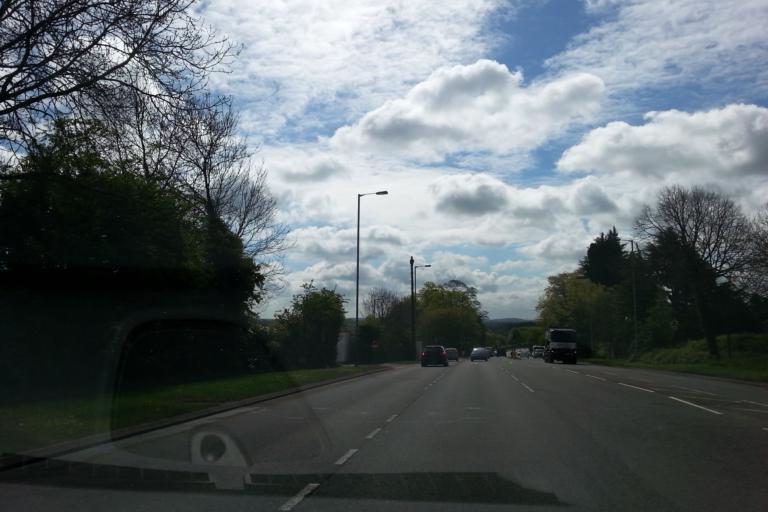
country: GB
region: England
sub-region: Staffordshire
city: Lichfield
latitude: 52.6934
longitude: -1.8498
